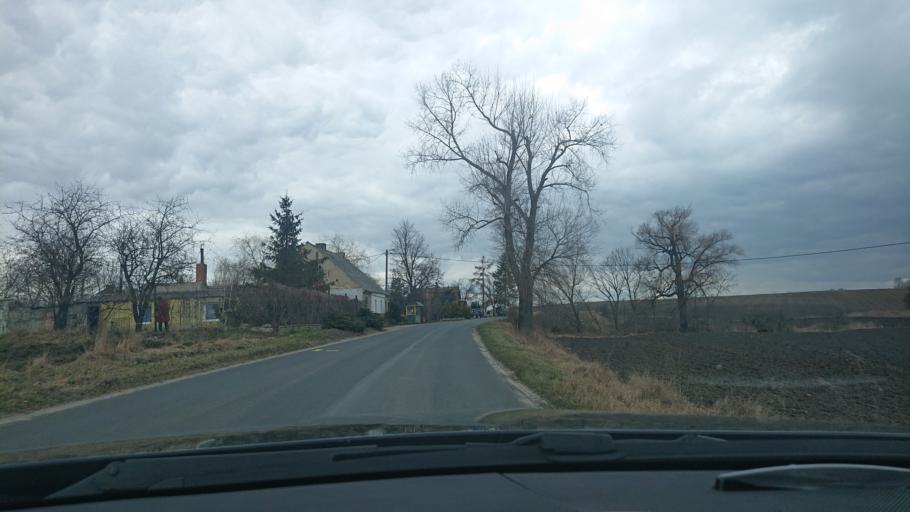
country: PL
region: Greater Poland Voivodeship
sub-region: Powiat gnieznienski
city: Gniezno
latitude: 52.5755
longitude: 17.6688
